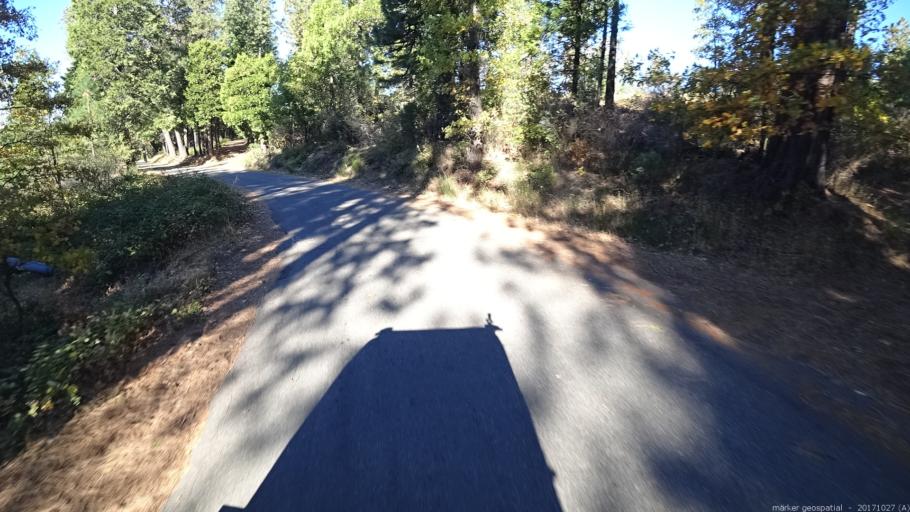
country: US
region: California
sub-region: Shasta County
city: Burney
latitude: 40.8607
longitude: -121.9186
